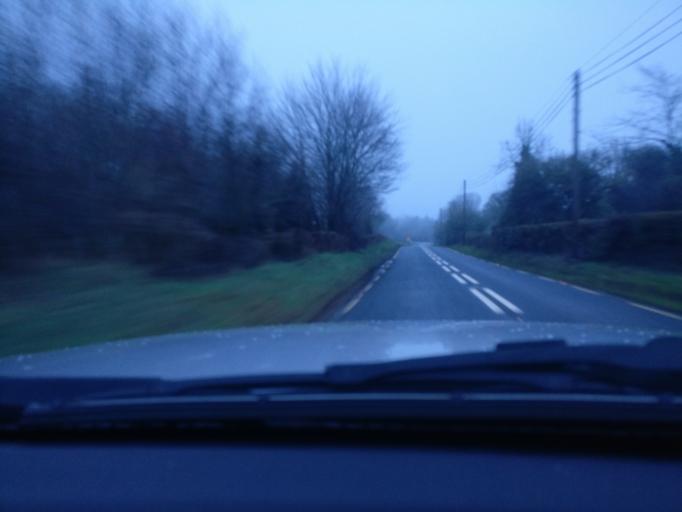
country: IE
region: Leinster
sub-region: An Mhi
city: Athboy
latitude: 53.6091
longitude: -6.9521
